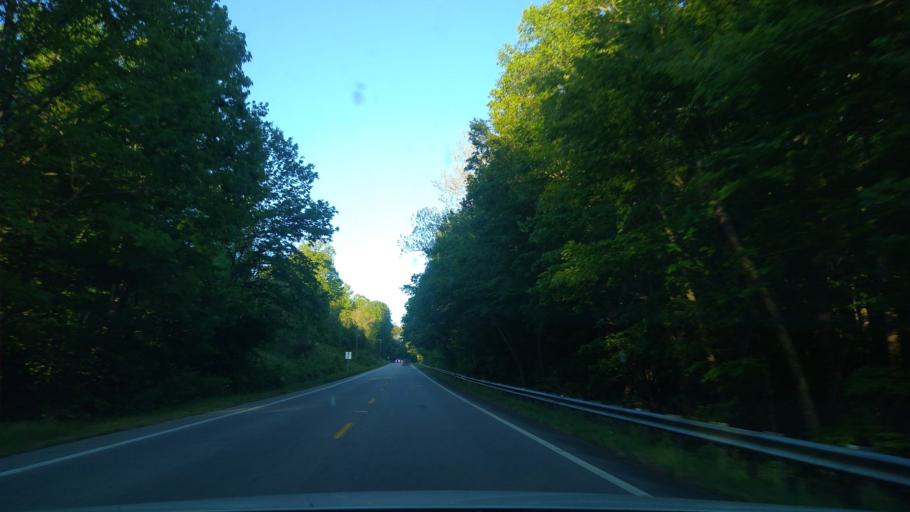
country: US
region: North Carolina
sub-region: Rockingham County
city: Reidsville
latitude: 36.3986
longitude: -79.5289
